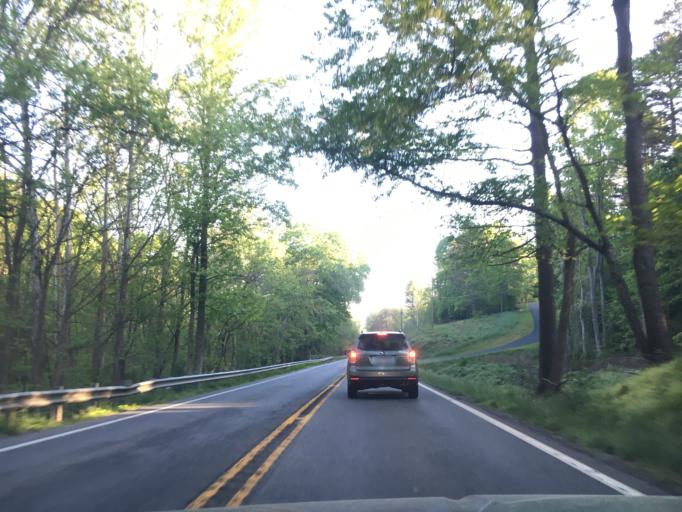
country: US
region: Virginia
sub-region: Campbell County
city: Rustburg
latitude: 37.2908
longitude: -79.1080
